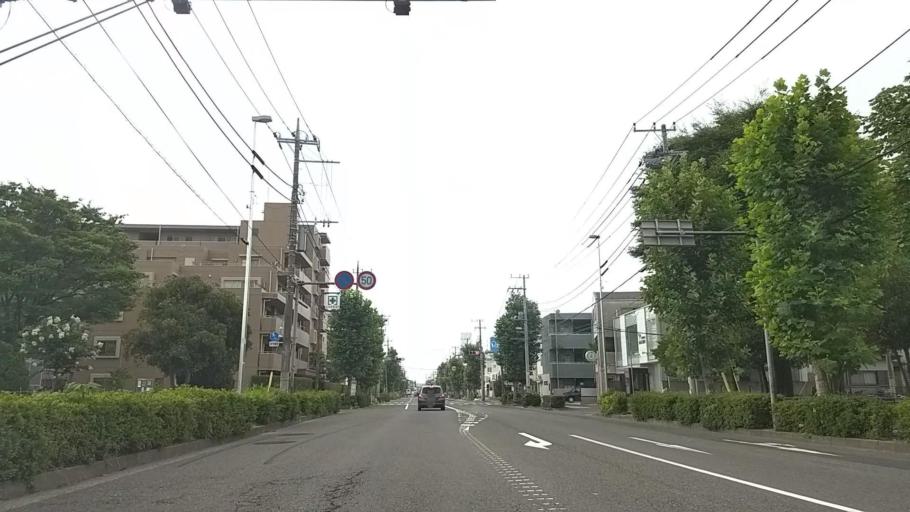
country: JP
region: Kanagawa
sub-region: Kawasaki-shi
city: Kawasaki
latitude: 35.5102
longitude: 139.6919
